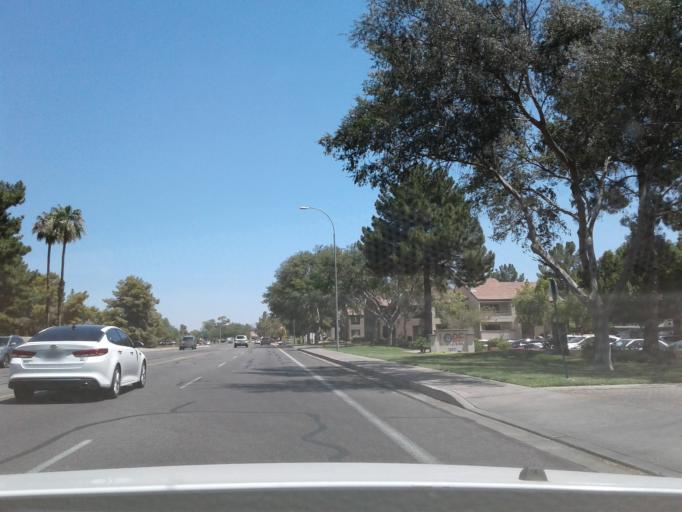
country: US
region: Arizona
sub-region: Maricopa County
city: Guadalupe
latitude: 33.3273
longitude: -111.9804
